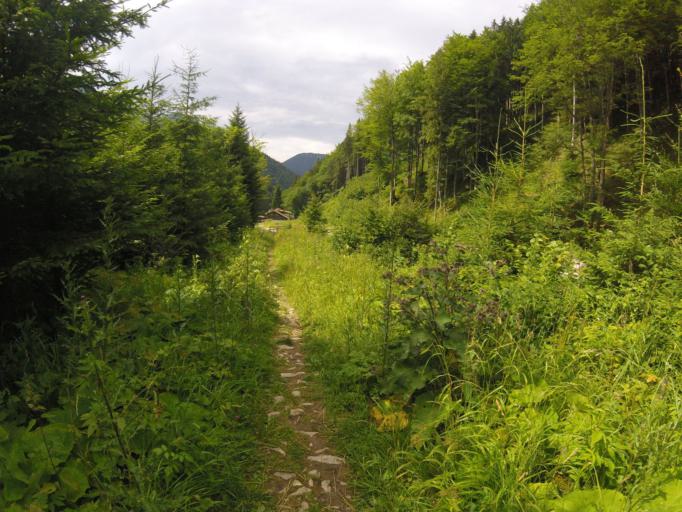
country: SK
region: Zilinsky
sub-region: Okres Zilina
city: Terchova
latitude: 49.2070
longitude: 19.0451
